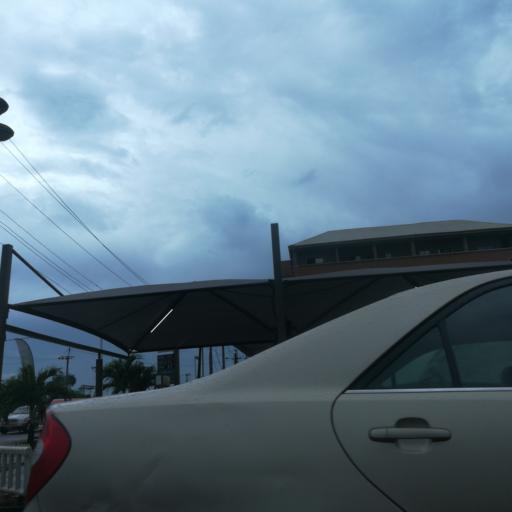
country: NG
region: Lagos
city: Ebute Metta
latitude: 6.4902
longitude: 3.3799
